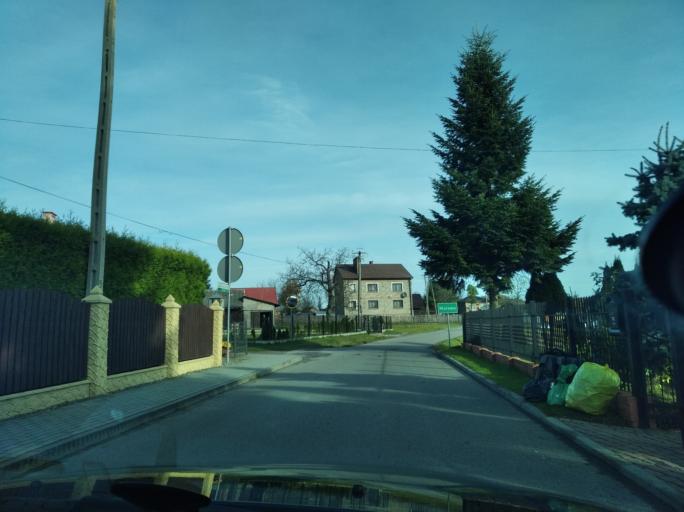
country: PL
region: Subcarpathian Voivodeship
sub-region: Powiat rzeszowski
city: Krasne
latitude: 50.0100
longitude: 22.0941
